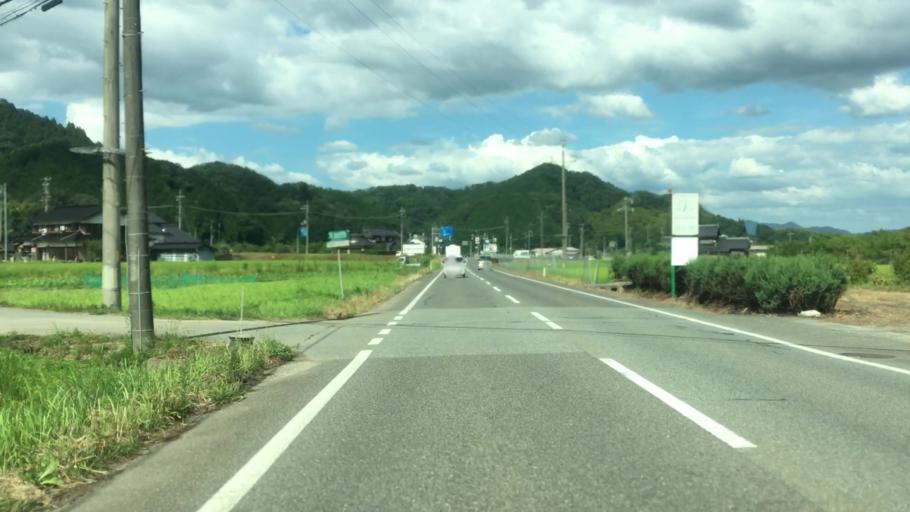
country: JP
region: Hyogo
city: Toyooka
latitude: 35.4624
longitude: 134.7401
